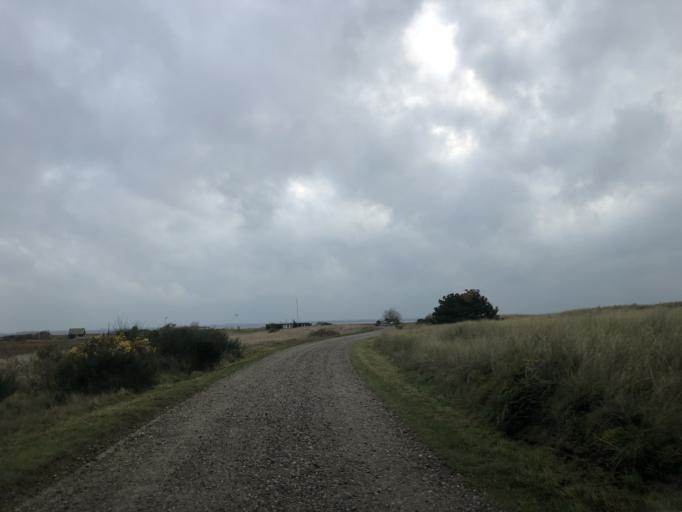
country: DK
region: Central Jutland
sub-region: Holstebro Kommune
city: Ulfborg
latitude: 56.3202
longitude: 8.2326
